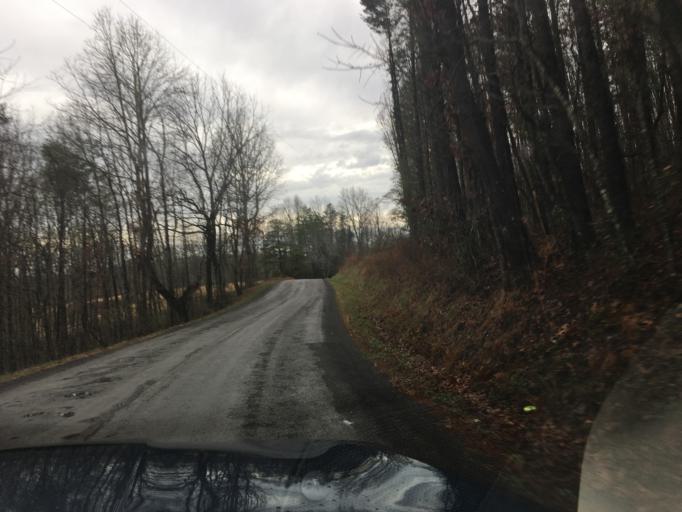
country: US
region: Georgia
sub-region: Fannin County
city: McCaysville
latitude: 35.1252
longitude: -84.3123
